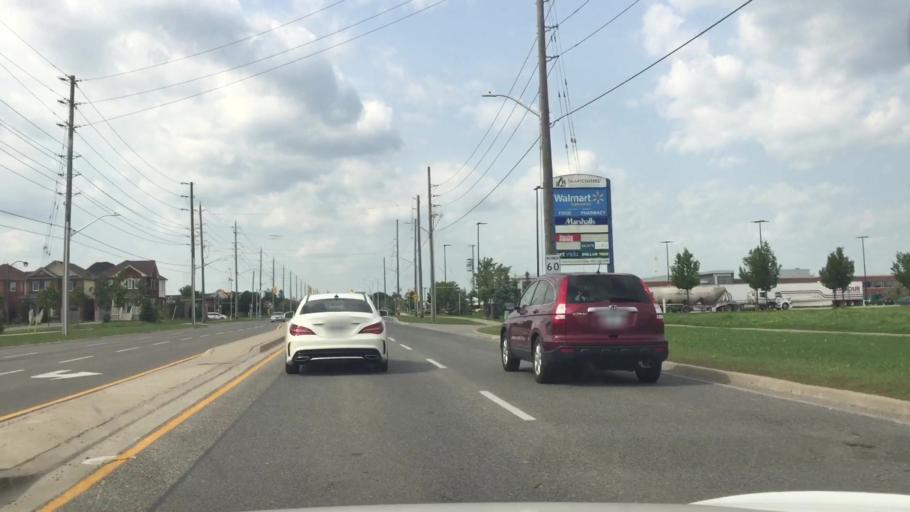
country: CA
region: Ontario
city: Oshawa
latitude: 43.9428
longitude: -78.8508
